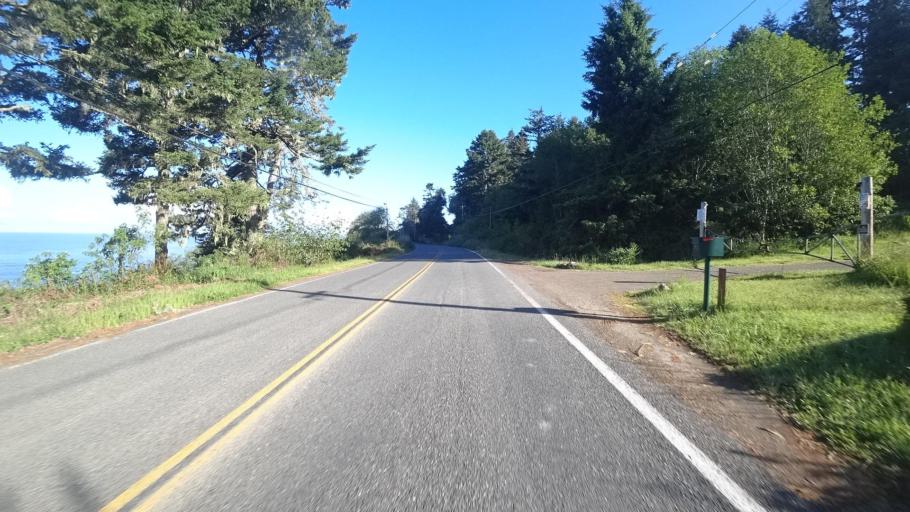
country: US
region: California
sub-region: Humboldt County
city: Westhaven-Moonstone
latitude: 41.0990
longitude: -124.1580
